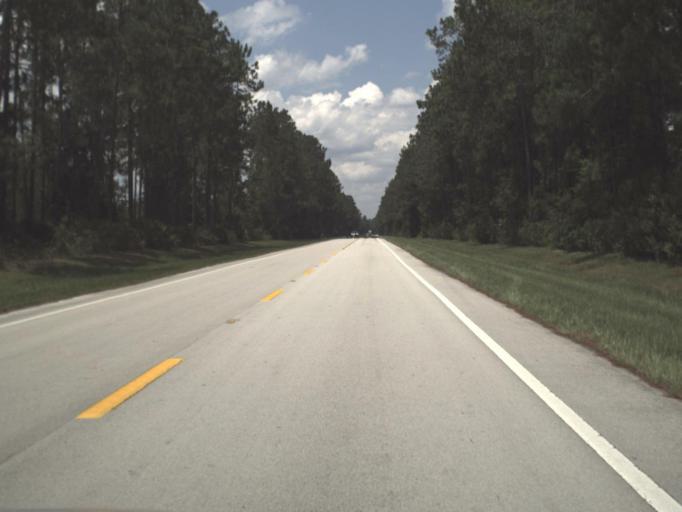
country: US
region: Florida
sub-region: Baker County
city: Macclenny
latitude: 30.1561
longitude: -82.1850
